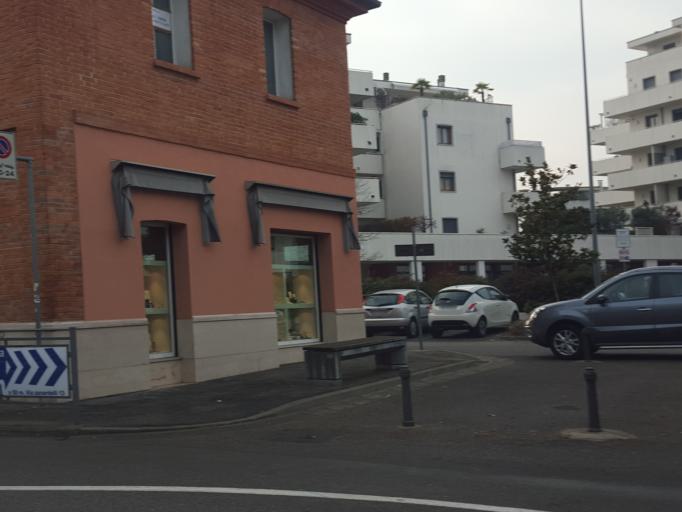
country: IT
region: Veneto
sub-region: Provincia di Vicenza
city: Vicenza
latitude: 45.5499
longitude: 11.5249
